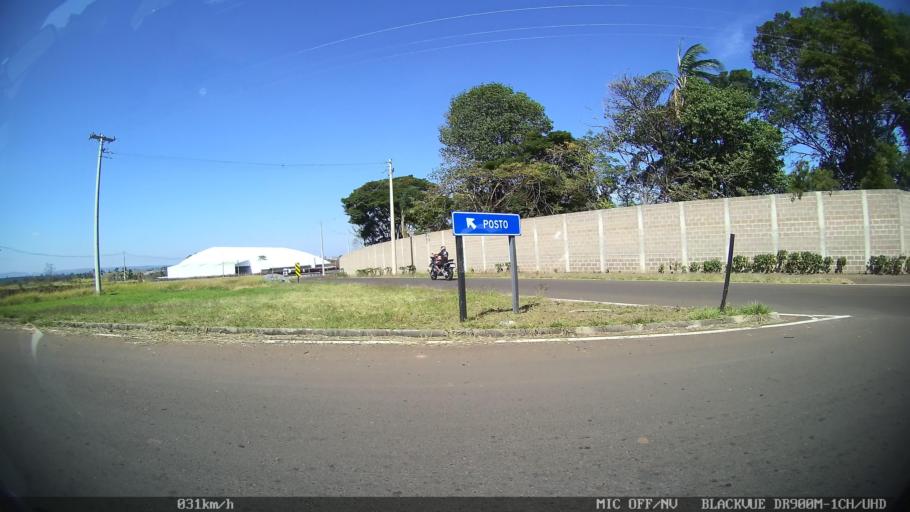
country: BR
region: Sao Paulo
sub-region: Franca
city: Franca
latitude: -20.4598
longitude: -47.4168
